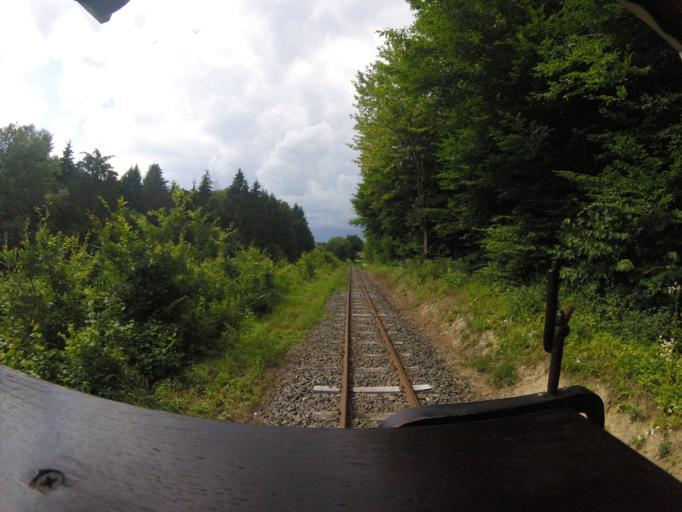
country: HU
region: Zala
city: Becsehely
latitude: 46.5046
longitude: 16.7340
